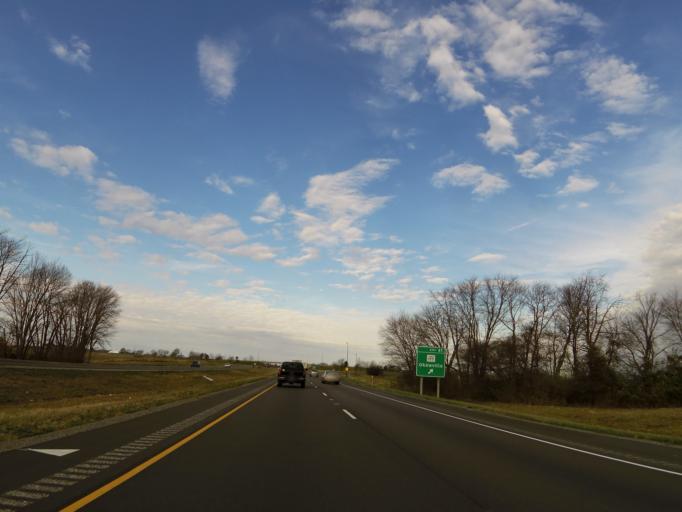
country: US
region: Illinois
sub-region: Washington County
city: Okawville
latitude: 38.4363
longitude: -89.5234
